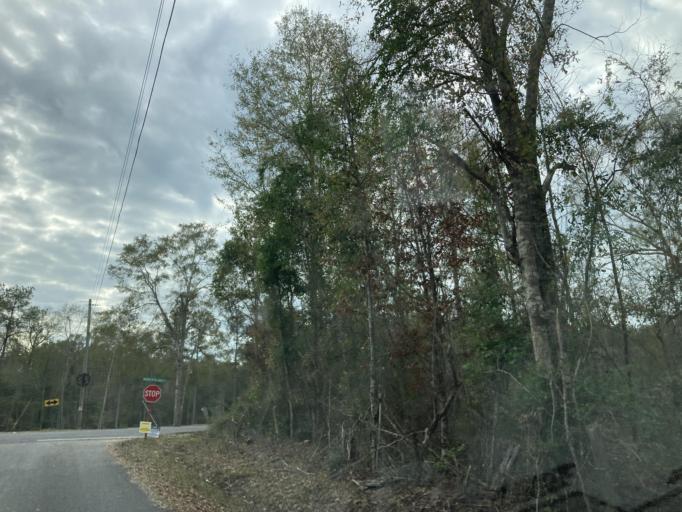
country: US
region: Mississippi
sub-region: Perry County
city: New Augusta
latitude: 31.0691
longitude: -89.1504
